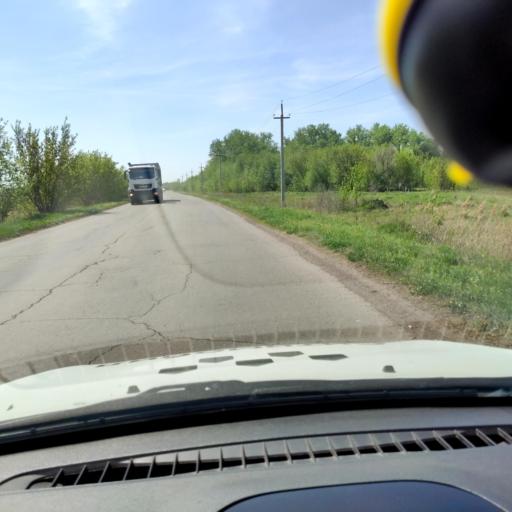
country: RU
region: Samara
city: Tol'yatti
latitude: 53.6436
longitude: 49.3163
